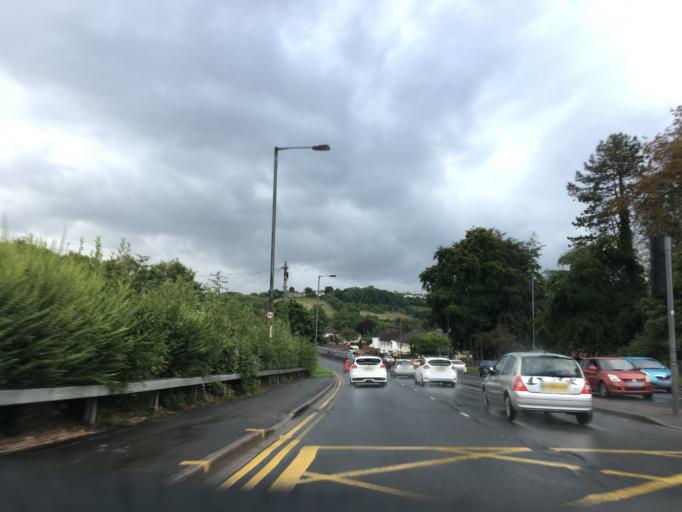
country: GB
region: Wales
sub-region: Newport
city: Newport
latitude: 51.6056
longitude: -3.0086
